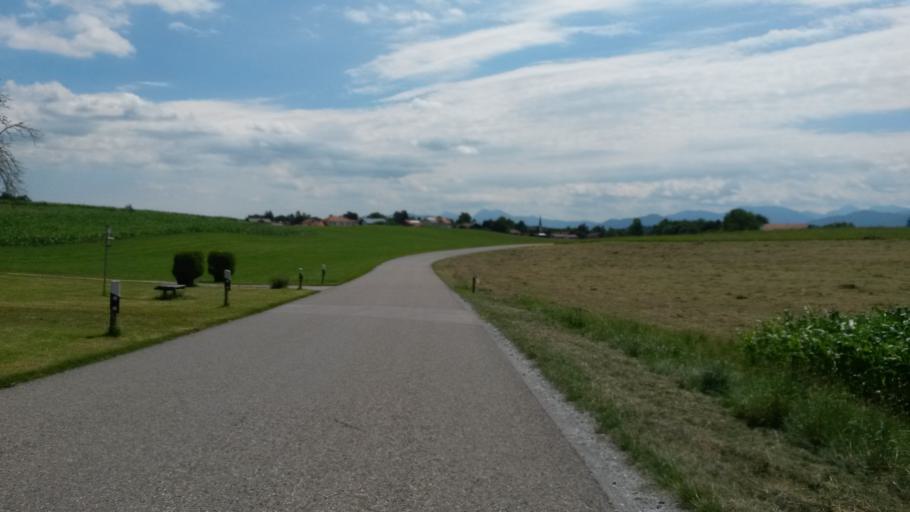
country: DE
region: Bavaria
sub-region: Upper Bavaria
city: Chieming
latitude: 47.8997
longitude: 12.5284
